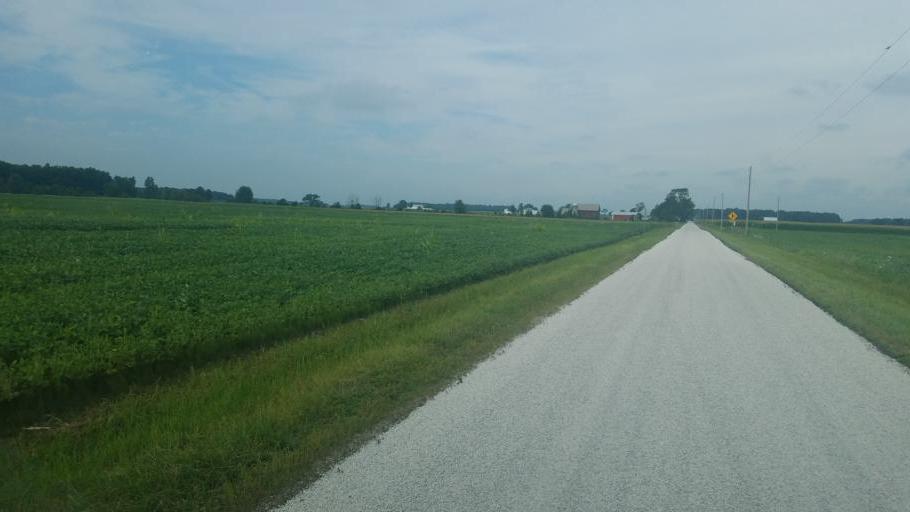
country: US
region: Ohio
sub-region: Morrow County
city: Cardington
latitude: 40.5139
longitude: -82.9833
